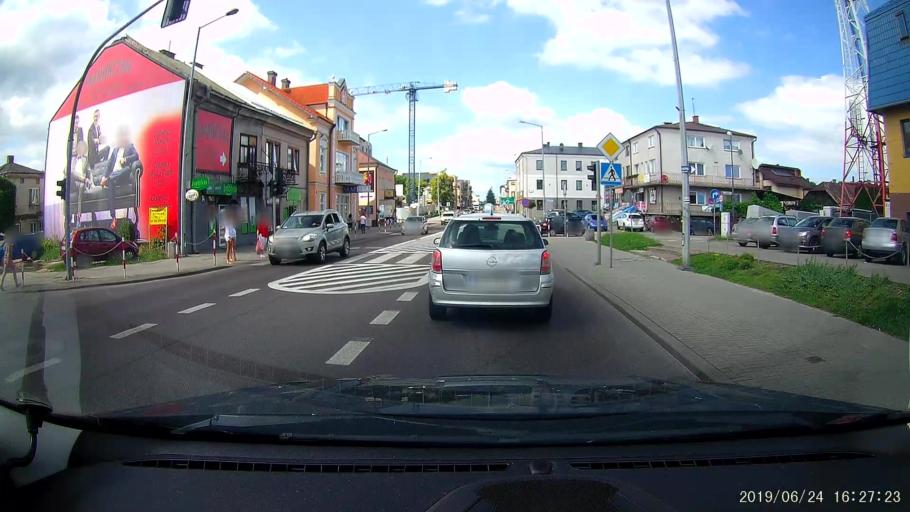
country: PL
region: Lublin Voivodeship
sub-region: Powiat tomaszowski
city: Tomaszow Lubelski
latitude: 50.4504
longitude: 23.4177
